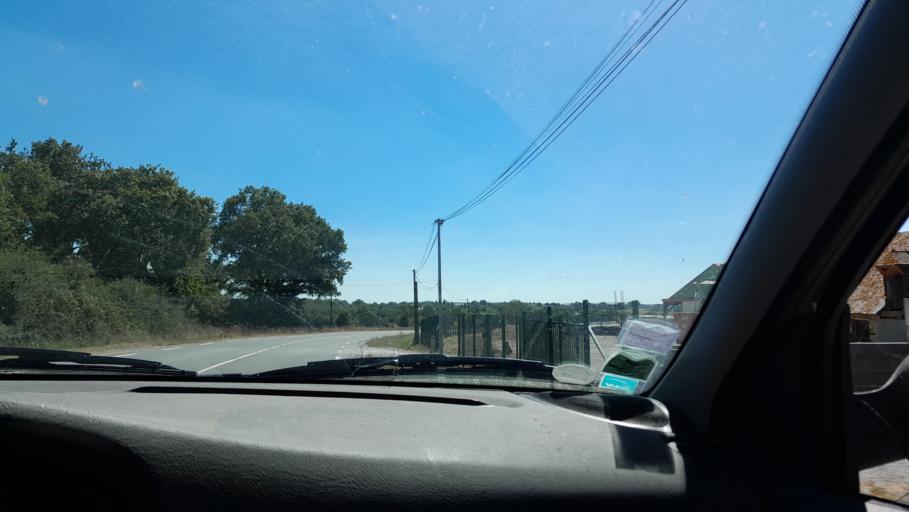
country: FR
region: Pays de la Loire
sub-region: Departement de la Loire-Atlantique
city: Saint-Mars-la-Jaille
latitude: 47.6153
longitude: -1.1987
